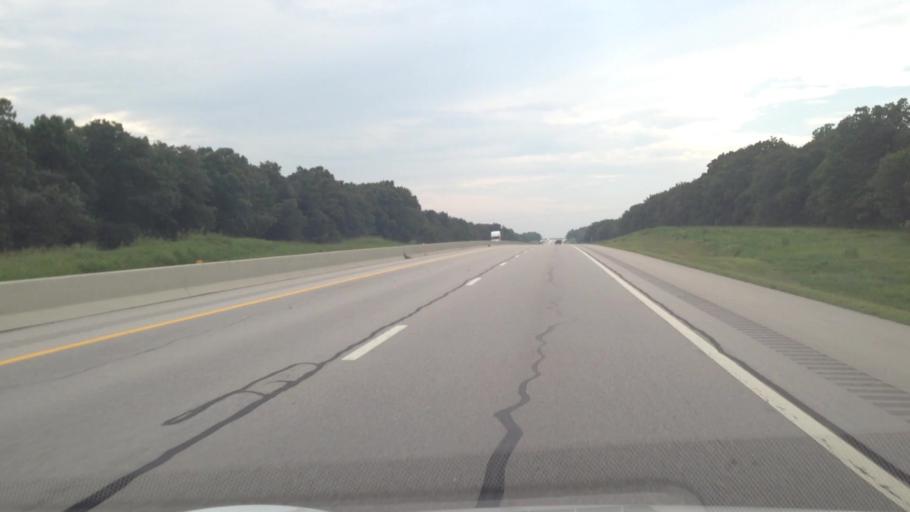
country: US
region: Kansas
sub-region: Cherokee County
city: Baxter Springs
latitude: 36.9391
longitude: -94.6956
